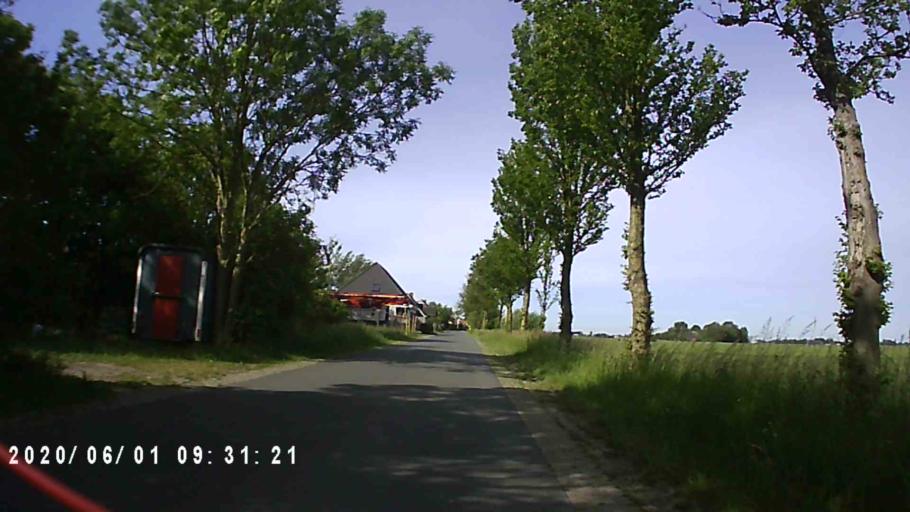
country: NL
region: Friesland
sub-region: Gemeente Leeuwarderadeel
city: Stiens
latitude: 53.2638
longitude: 5.7340
